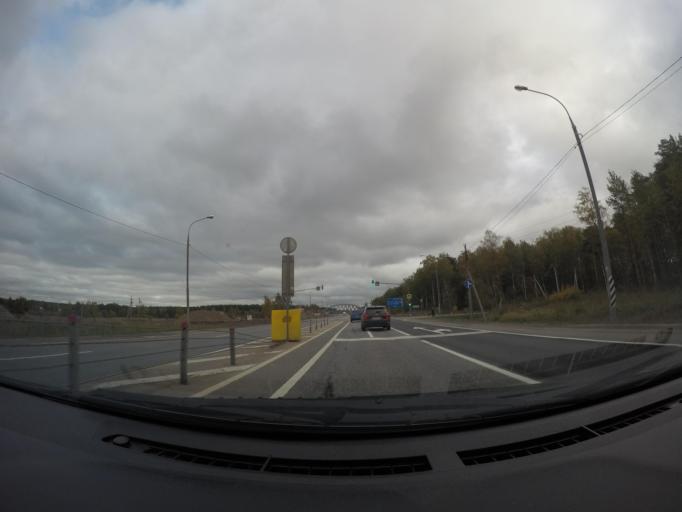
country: RU
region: Moskovskaya
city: Chupryakovo
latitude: 55.5671
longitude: 36.6593
